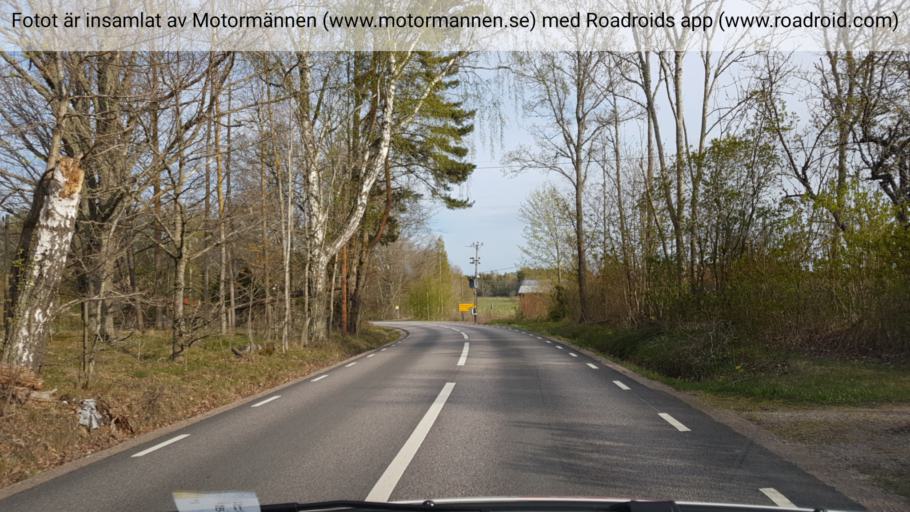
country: SE
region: Kalmar
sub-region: Vasterviks Kommun
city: Vaestervik
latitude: 57.9071
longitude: 16.6633
